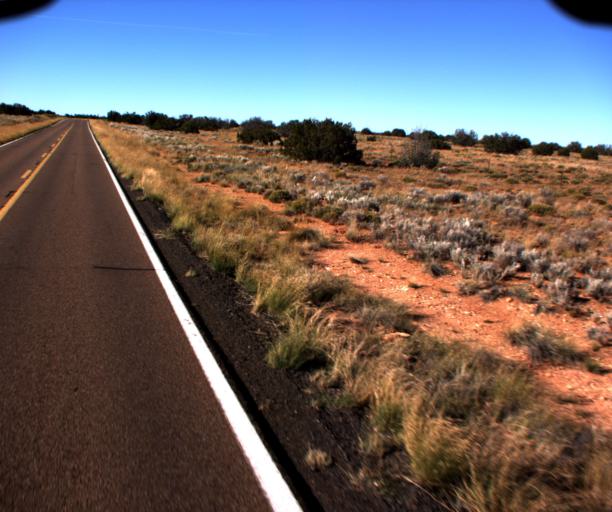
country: US
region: Arizona
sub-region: Navajo County
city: Holbrook
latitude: 34.6954
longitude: -110.3059
